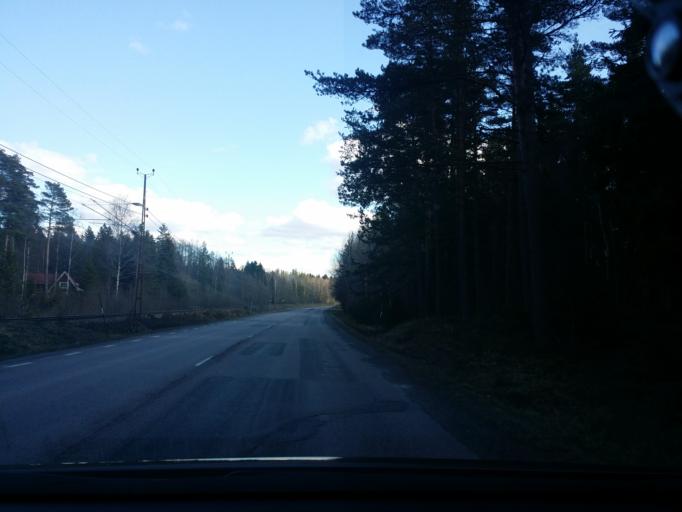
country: SE
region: Vaestmanland
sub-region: Sala Kommun
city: Sala
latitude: 59.9482
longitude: 16.5388
